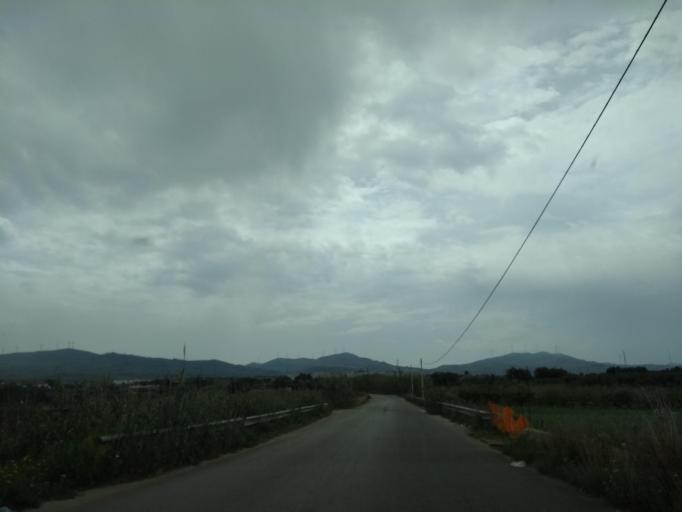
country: IT
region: Sicily
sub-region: Palermo
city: Partinico
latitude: 38.0071
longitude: 13.0683
